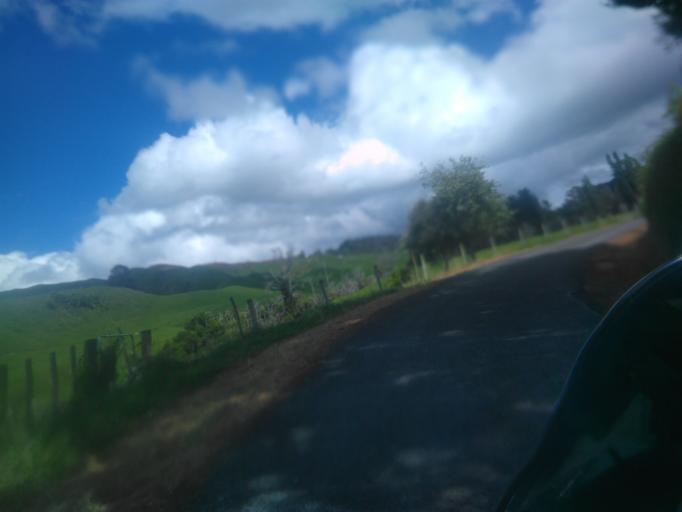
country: NZ
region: Hawke's Bay
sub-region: Wairoa District
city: Wairoa
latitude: -38.7584
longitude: 177.5958
